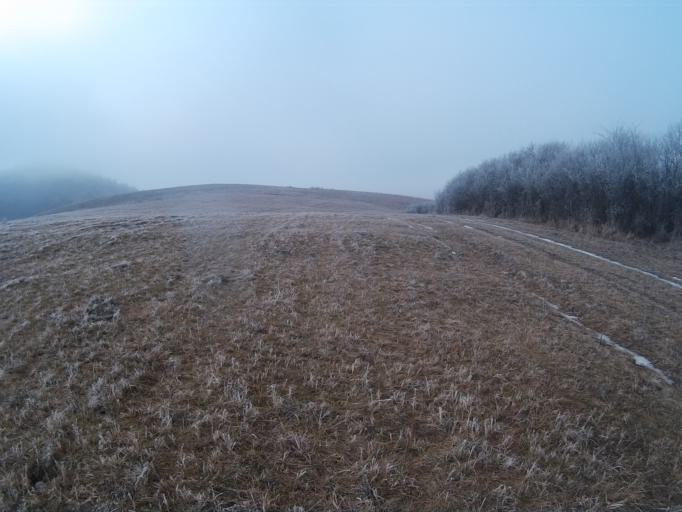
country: HU
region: Nograd
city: Tar
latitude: 47.9947
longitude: 19.7099
